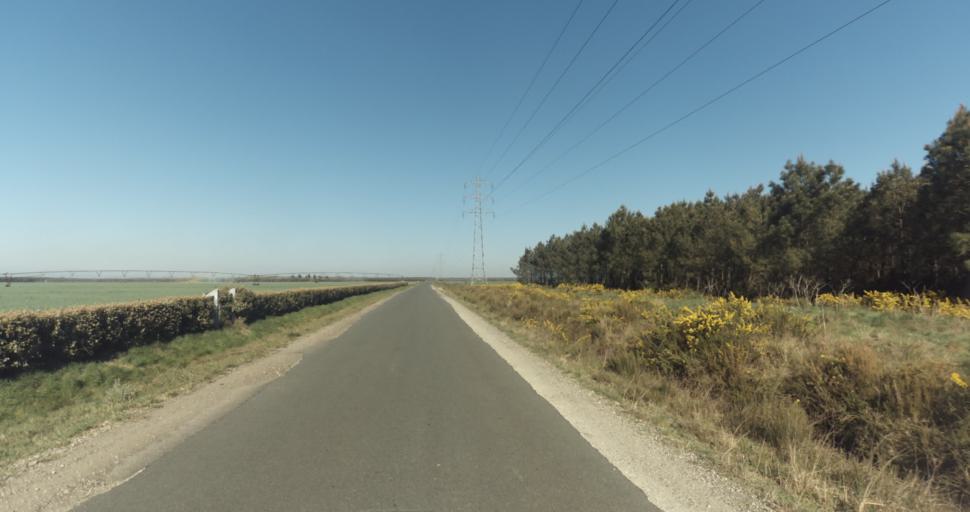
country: FR
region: Aquitaine
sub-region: Departement de la Gironde
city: Marcheprime
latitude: 44.7442
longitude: -0.8311
